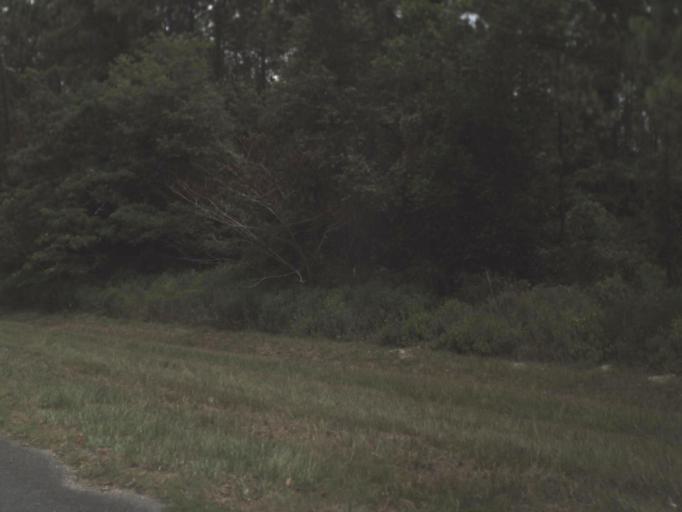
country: US
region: Florida
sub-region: Taylor County
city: Perry
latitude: 30.0811
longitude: -83.5100
